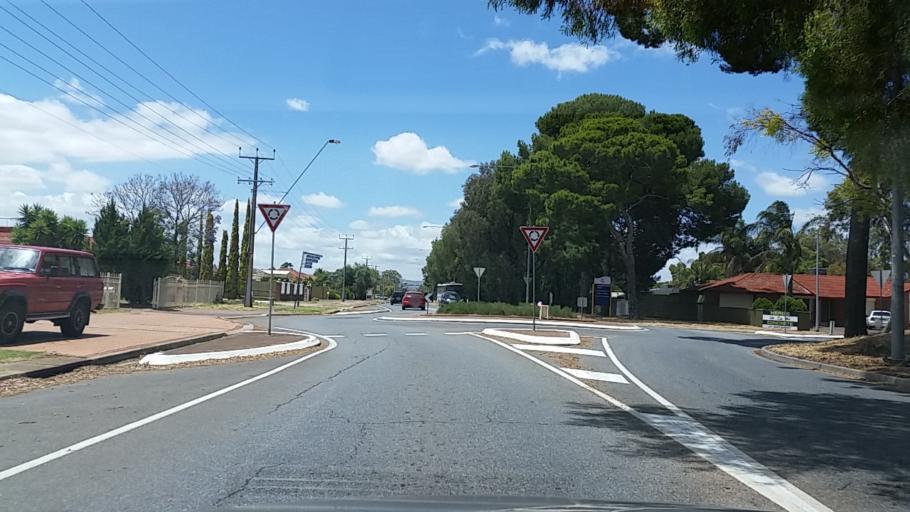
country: AU
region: South Australia
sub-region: Salisbury
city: Salisbury
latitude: -34.7699
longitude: 138.6110
